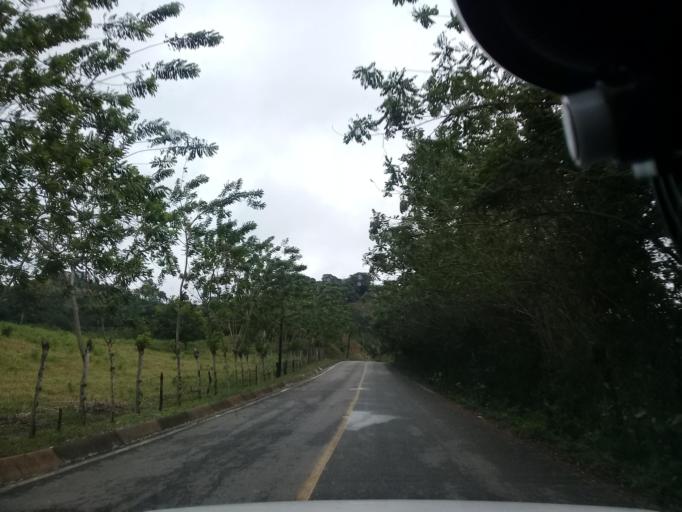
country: MX
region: Veracruz
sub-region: Chalma
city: San Pedro Coyutla
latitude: 21.2155
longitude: -98.4279
